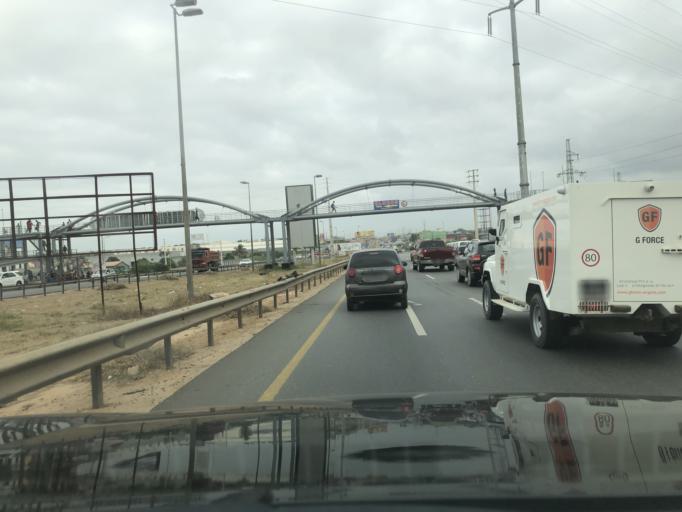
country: AO
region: Luanda
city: Luanda
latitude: -8.9748
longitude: 13.2117
